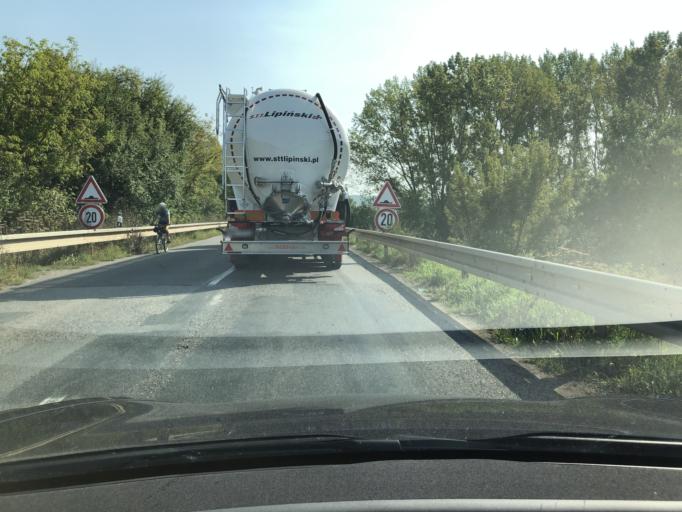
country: CZ
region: South Moravian
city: Drnholec
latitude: 48.8554
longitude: 16.4891
